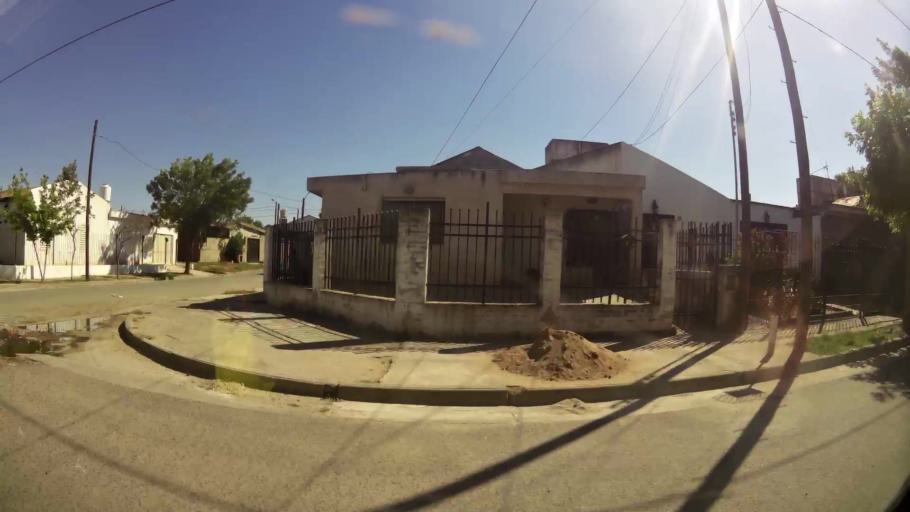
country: AR
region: Cordoba
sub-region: Departamento de Capital
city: Cordoba
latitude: -31.3656
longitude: -64.1650
